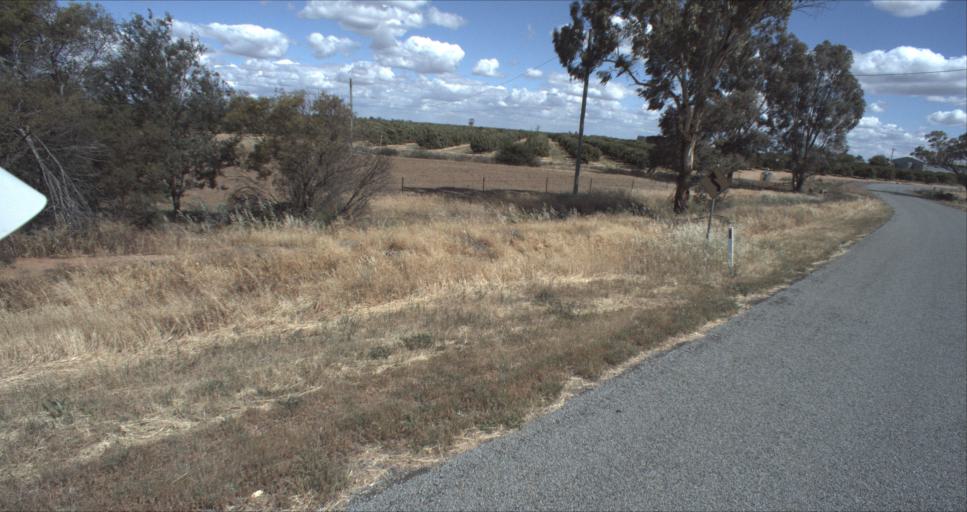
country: AU
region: New South Wales
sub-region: Leeton
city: Leeton
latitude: -34.5172
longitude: 146.2291
